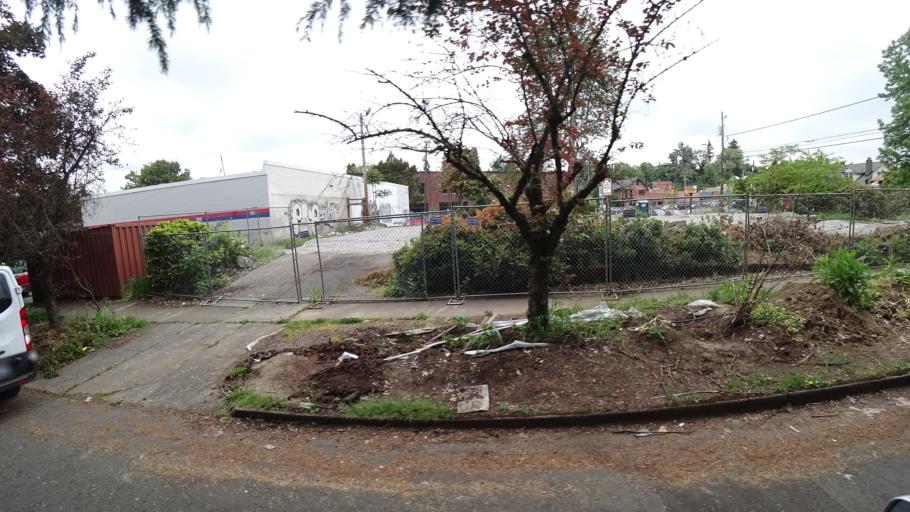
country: US
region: Oregon
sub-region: Multnomah County
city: Portland
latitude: 45.5390
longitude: -122.6114
